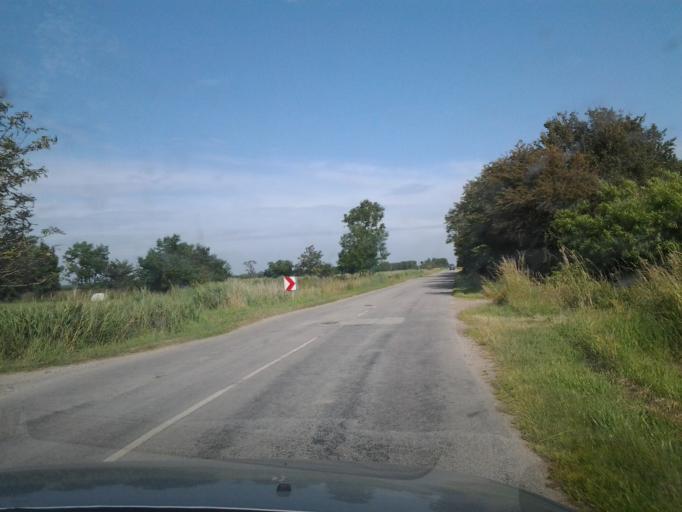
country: DE
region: Schleswig-Holstein
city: Aventoft
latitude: 54.9221
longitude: 8.7872
